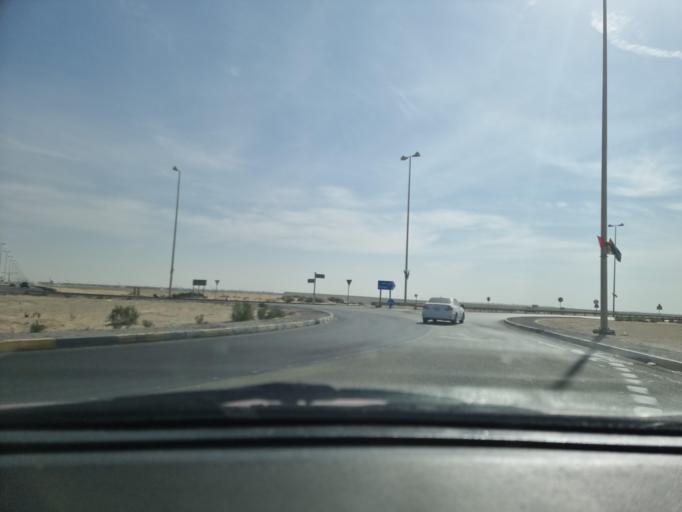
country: AE
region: Abu Dhabi
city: Abu Dhabi
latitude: 24.3601
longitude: 54.6669
